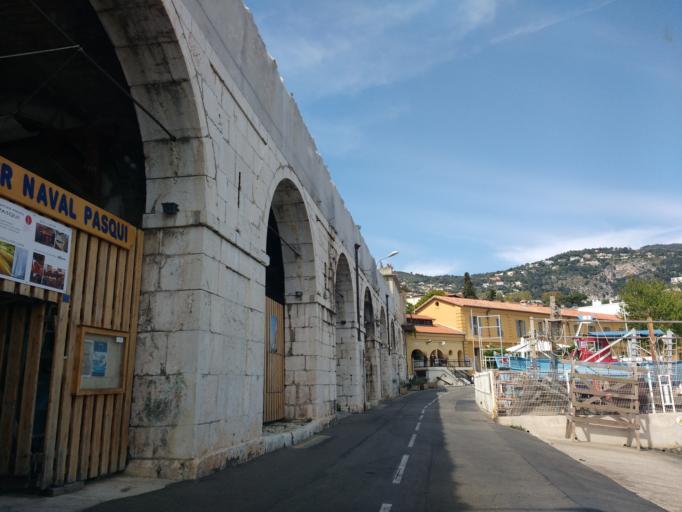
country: FR
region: Provence-Alpes-Cote d'Azur
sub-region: Departement des Alpes-Maritimes
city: Villefranche-sur-Mer
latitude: 43.6979
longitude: 7.3068
